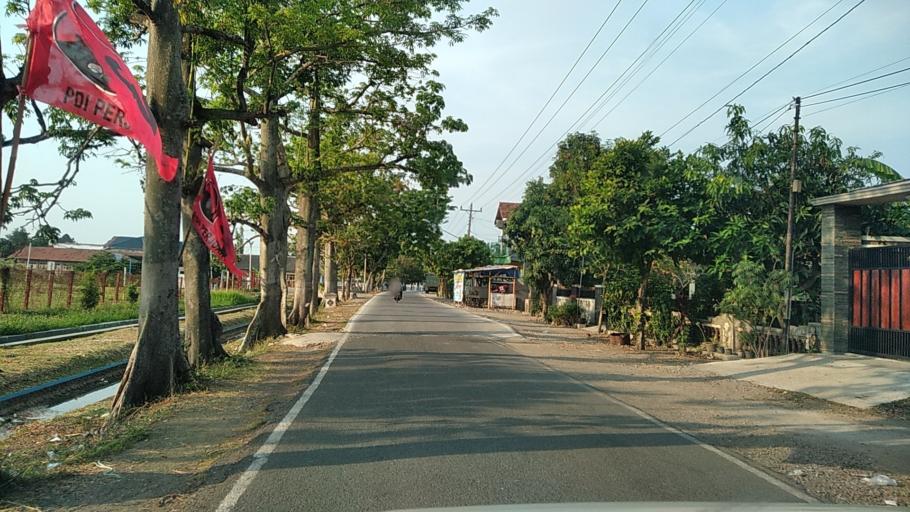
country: ID
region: Central Java
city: Semarang
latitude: -6.9687
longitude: 110.2985
